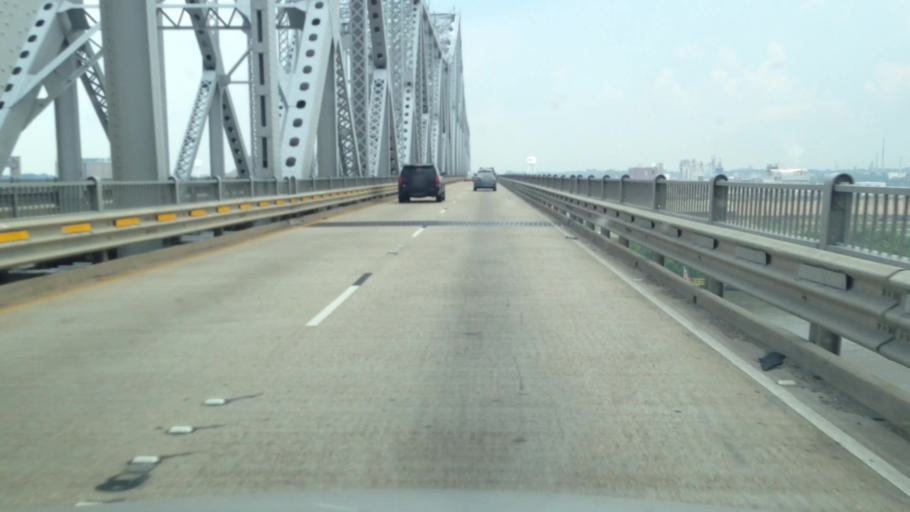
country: US
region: Louisiana
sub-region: West Baton Rouge Parish
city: Port Allen
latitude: 30.5069
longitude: -91.1967
